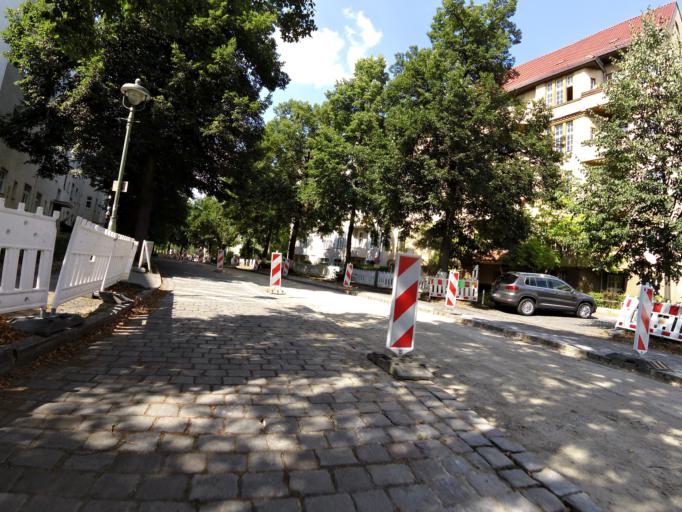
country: DE
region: Berlin
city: Lankwitz
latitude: 52.4452
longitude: 13.3462
